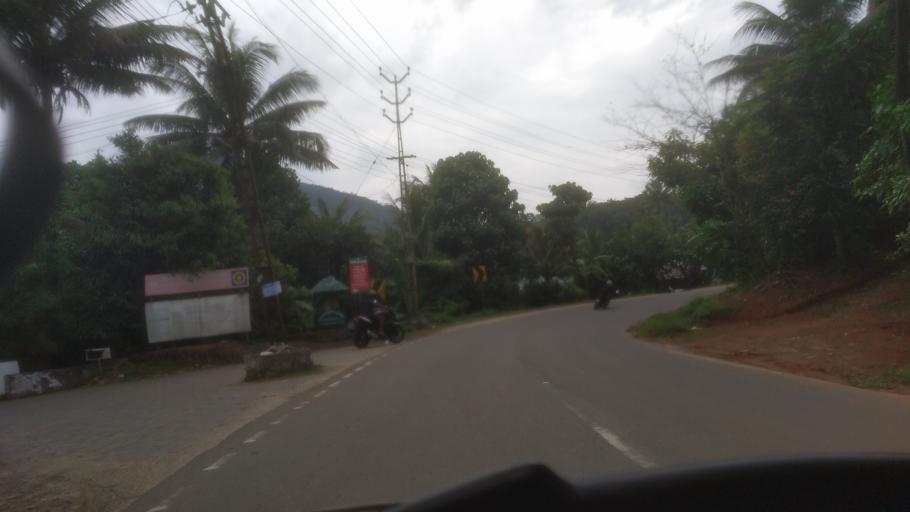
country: IN
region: Kerala
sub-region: Idukki
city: Munnar
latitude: 10.0052
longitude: 76.9663
